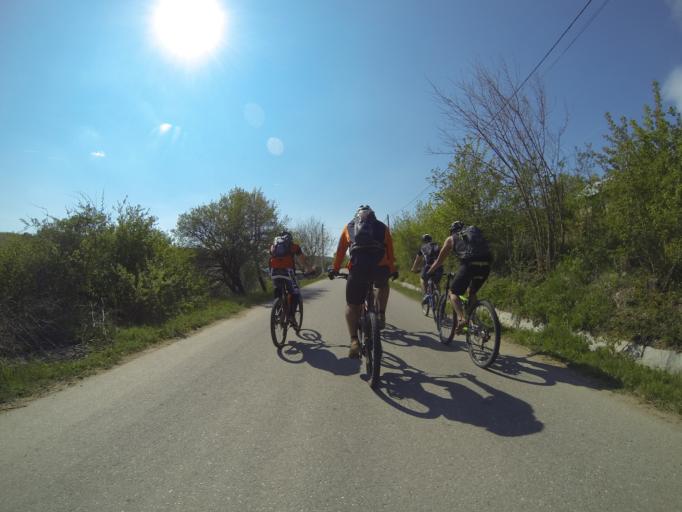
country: RO
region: Gorj
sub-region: Comuna Crusetu
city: Crusetu
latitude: 44.6182
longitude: 23.6646
